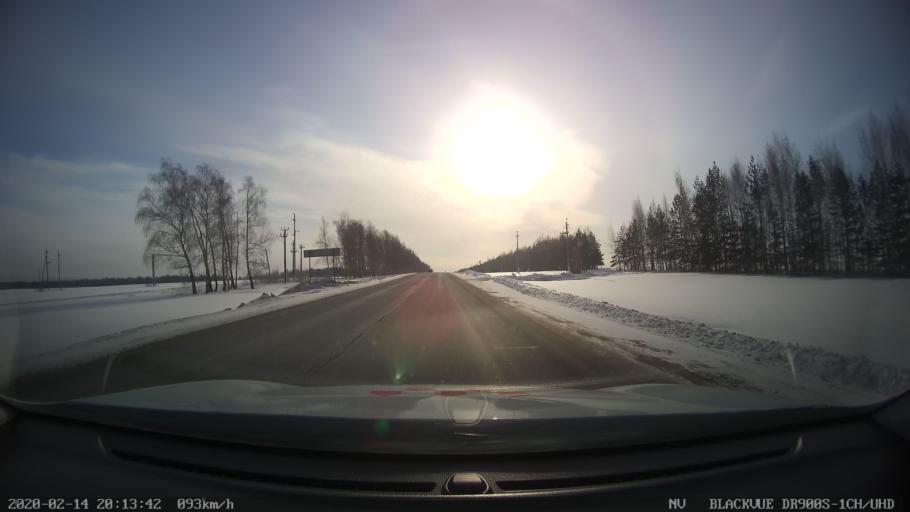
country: RU
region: Tatarstan
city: Verkhniy Uslon
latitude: 55.6544
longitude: 48.8639
